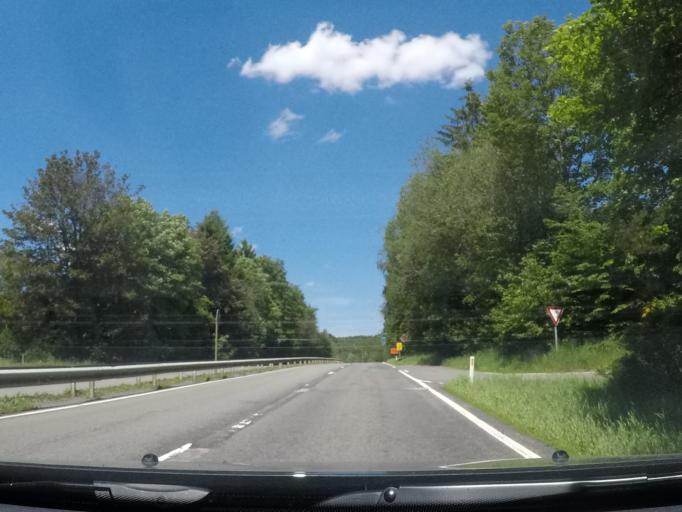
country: BE
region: Wallonia
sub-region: Province du Luxembourg
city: Saint-Hubert
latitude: 50.0296
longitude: 5.3847
